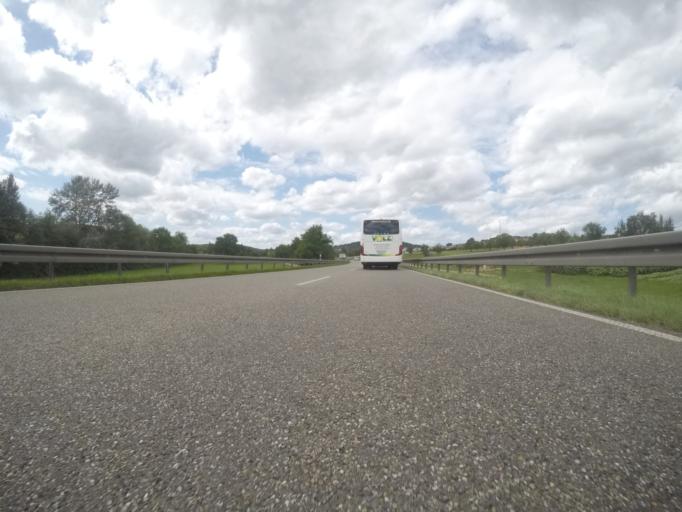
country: DE
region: Baden-Wuerttemberg
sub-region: Karlsruhe Region
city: Simmozheim
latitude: 48.7491
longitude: 8.8277
